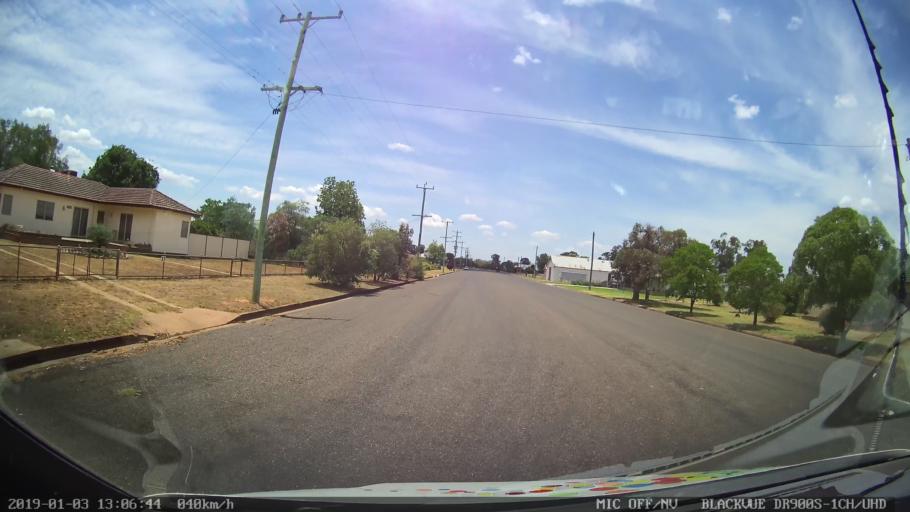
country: AU
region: New South Wales
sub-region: Cabonne
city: Canowindra
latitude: -33.6148
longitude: 148.4326
